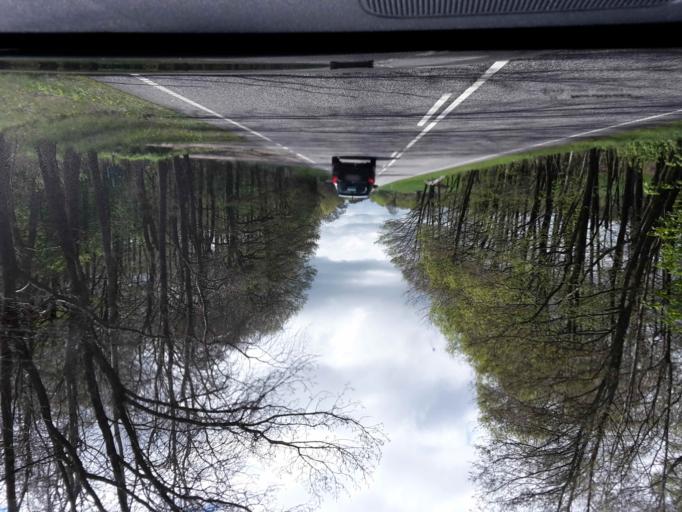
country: DK
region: Central Jutland
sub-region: Syddjurs Kommune
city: Ryomgard
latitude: 56.4284
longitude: 10.5456
